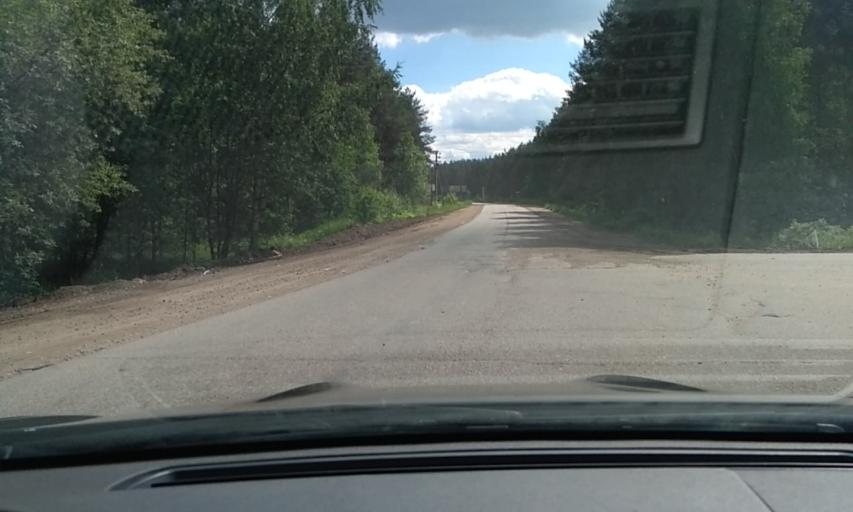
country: RU
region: Leningrad
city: Imeni Sverdlova
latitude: 59.8584
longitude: 30.6718
